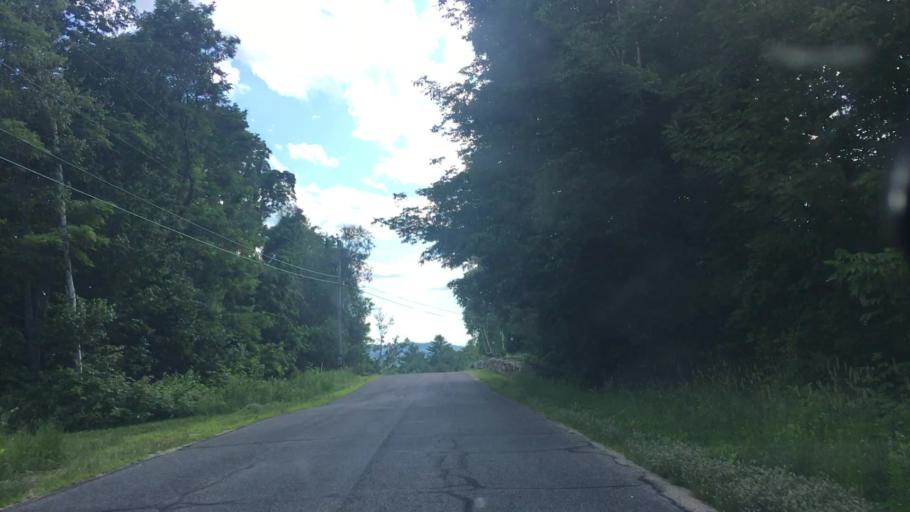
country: US
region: Maine
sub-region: Franklin County
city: Wilton
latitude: 44.6256
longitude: -70.2108
